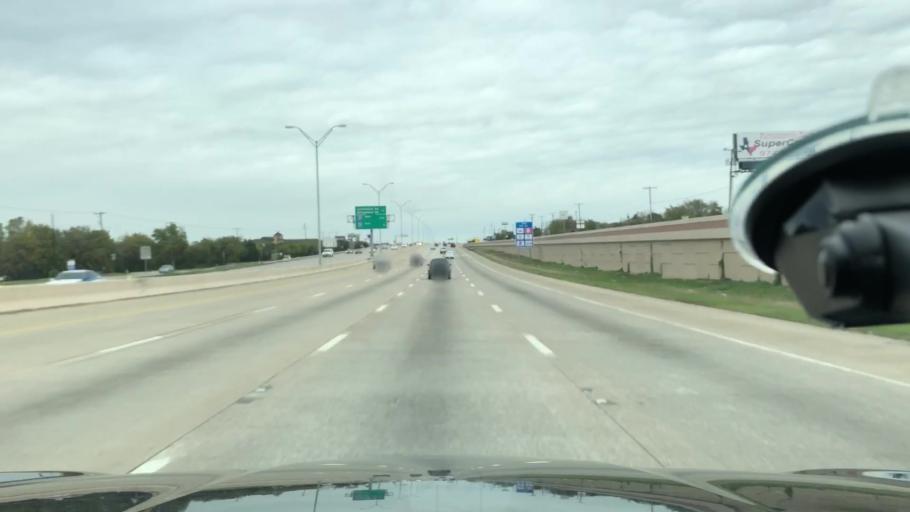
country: US
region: Texas
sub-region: Dallas County
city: DeSoto
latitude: 32.6114
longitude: -96.8229
